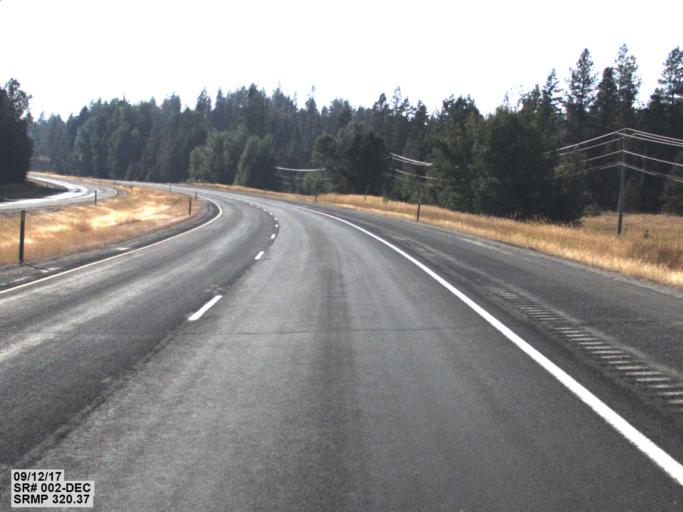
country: US
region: Washington
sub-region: Spokane County
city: Deer Park
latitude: 48.0987
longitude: -117.2979
